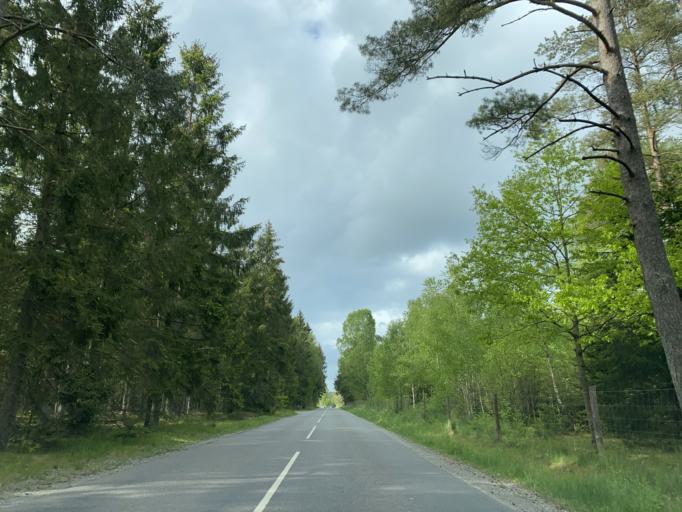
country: DK
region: Central Jutland
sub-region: Skanderborg Kommune
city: Ry
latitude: 56.0626
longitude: 9.6924
